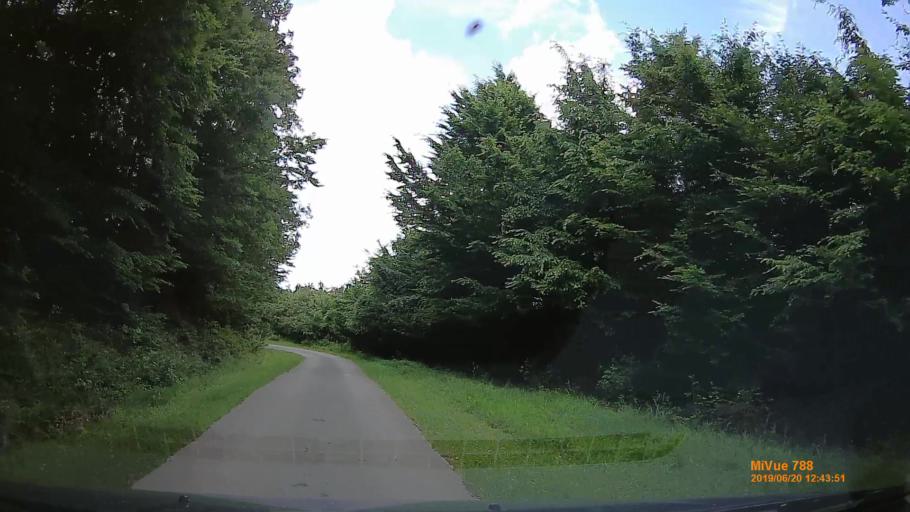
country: HU
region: Baranya
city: Hosszuheteny
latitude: 46.2032
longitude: 18.3553
